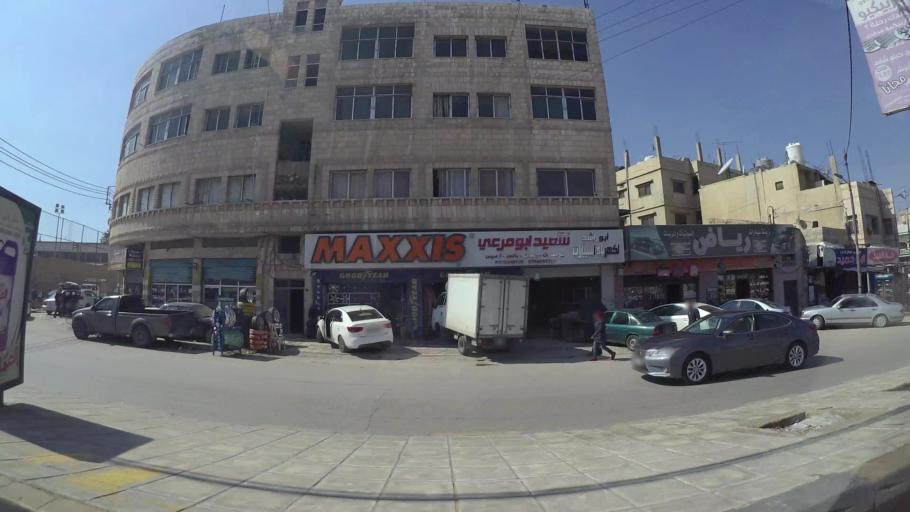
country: JO
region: Zarqa
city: Zarqa
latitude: 32.0689
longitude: 36.0974
